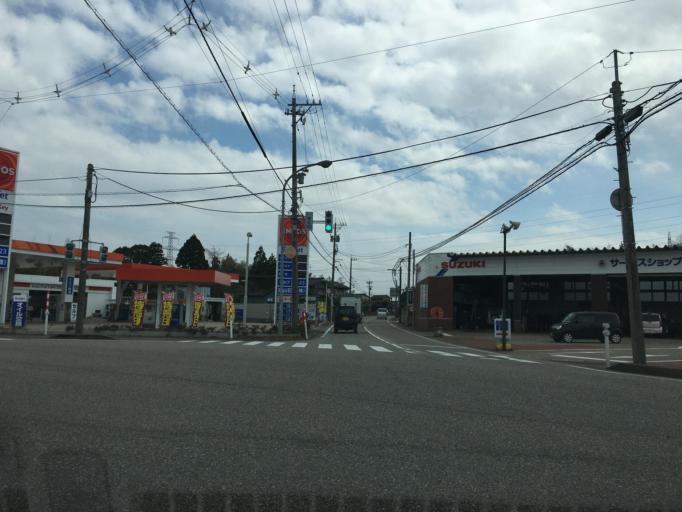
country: JP
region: Toyama
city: Kuragaki-kosugi
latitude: 36.6974
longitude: 137.1146
